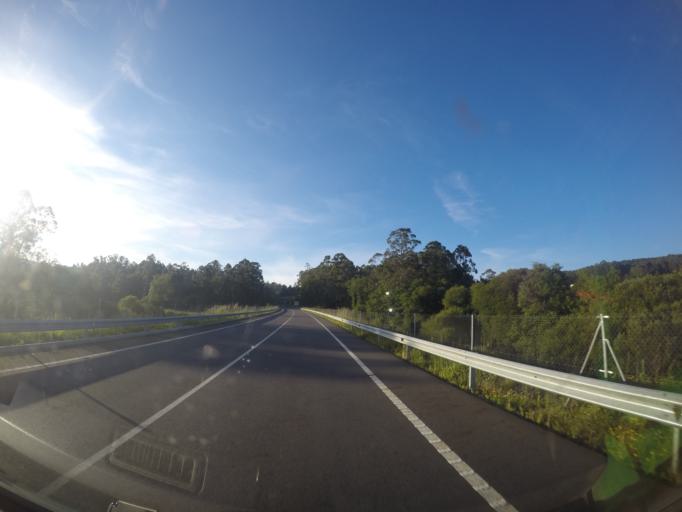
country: ES
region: Galicia
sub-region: Provincia da Coruna
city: Noia
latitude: 42.8055
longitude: -8.8888
